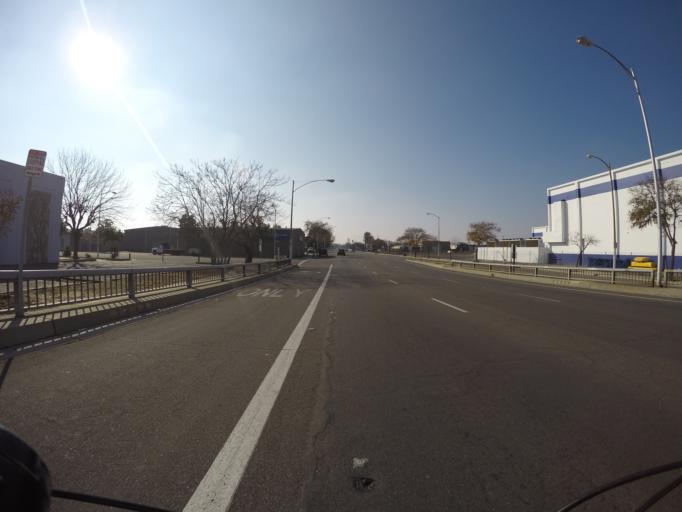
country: US
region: California
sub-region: Fresno County
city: Fresno
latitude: 36.7358
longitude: -119.7999
